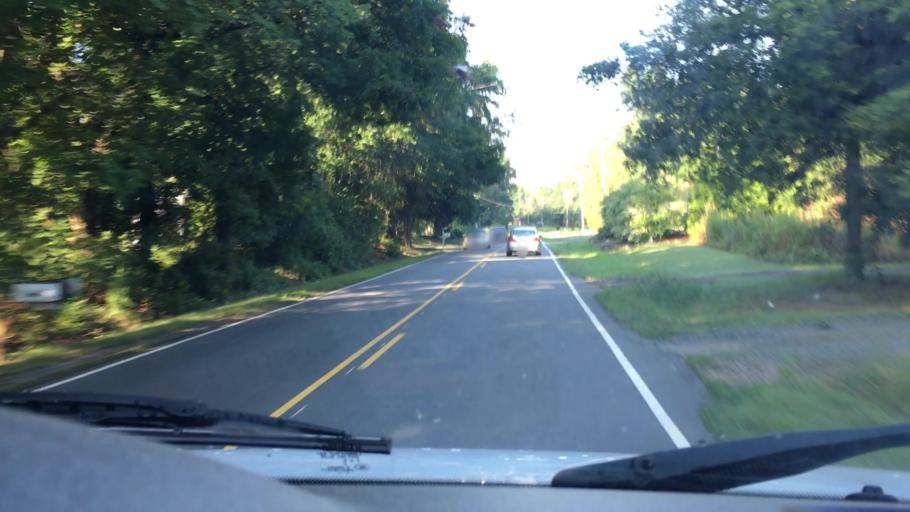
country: US
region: North Carolina
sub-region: Mecklenburg County
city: Huntersville
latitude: 35.4197
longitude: -80.9188
